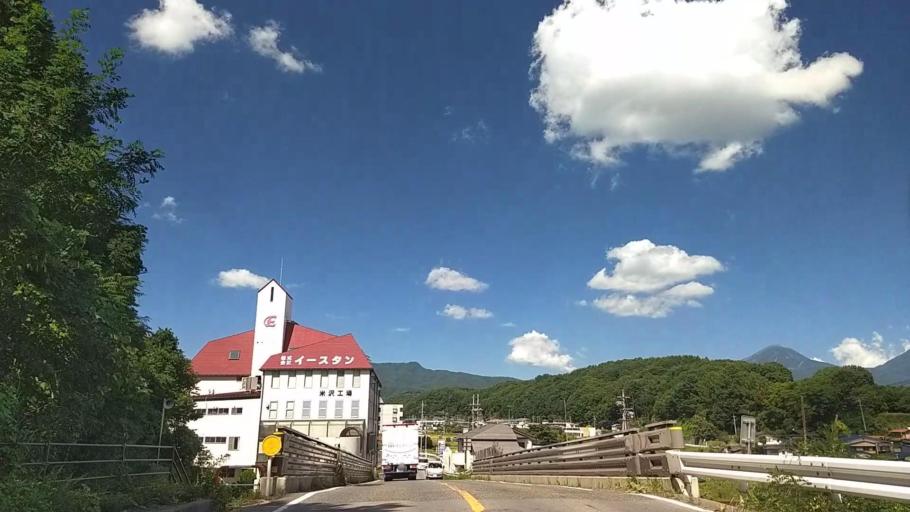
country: JP
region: Nagano
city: Chino
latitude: 36.0048
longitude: 138.1747
